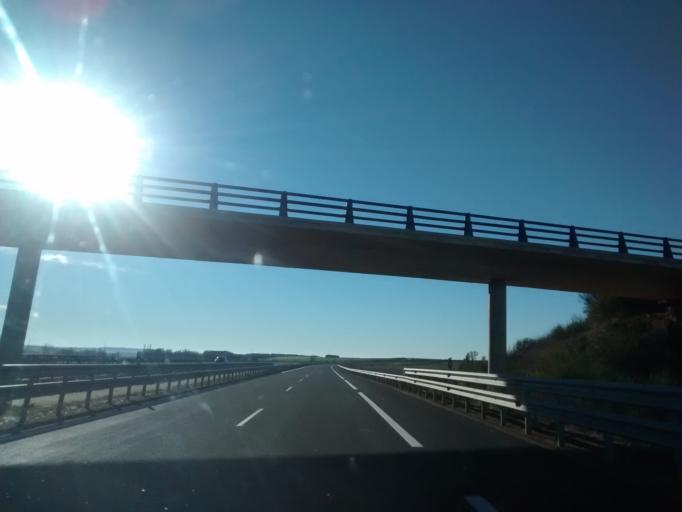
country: ES
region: Castille and Leon
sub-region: Provincia de Palencia
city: Espinosa de Villagonzalo
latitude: 42.4738
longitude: -4.3852
